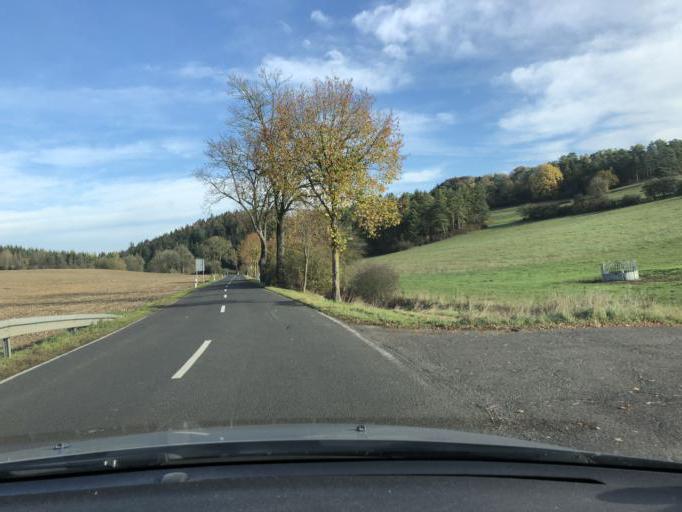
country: DE
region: Thuringia
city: Dingsleben
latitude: 50.4207
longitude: 10.6301
